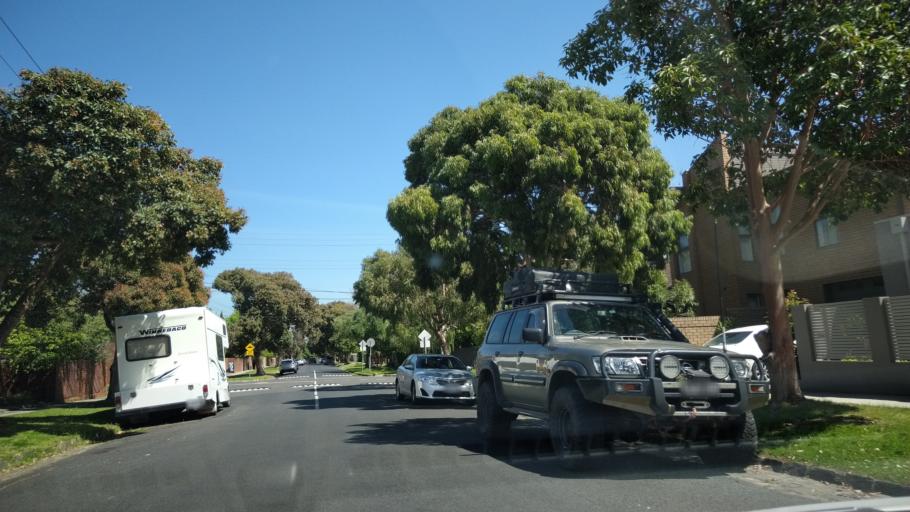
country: AU
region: Victoria
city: Ormond
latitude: -37.8944
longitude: 145.0327
